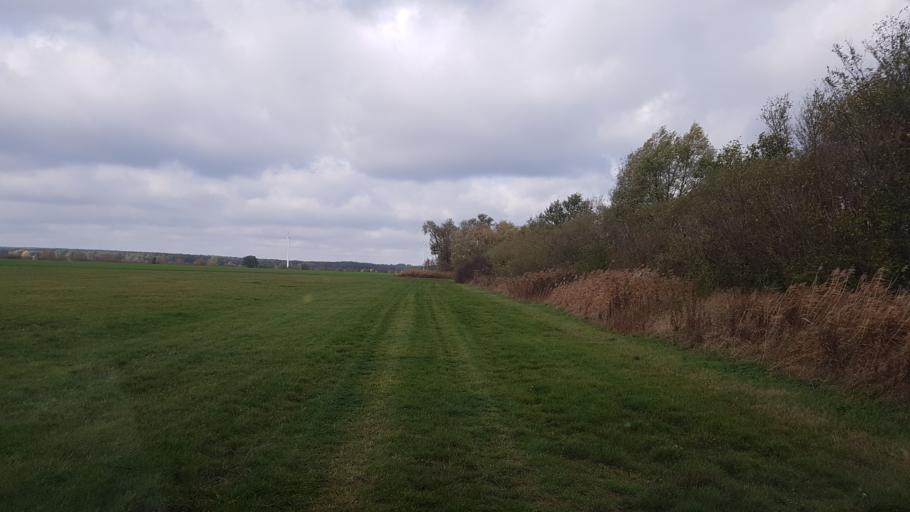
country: DE
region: Brandenburg
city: Schonborn
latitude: 51.5876
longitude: 13.5233
